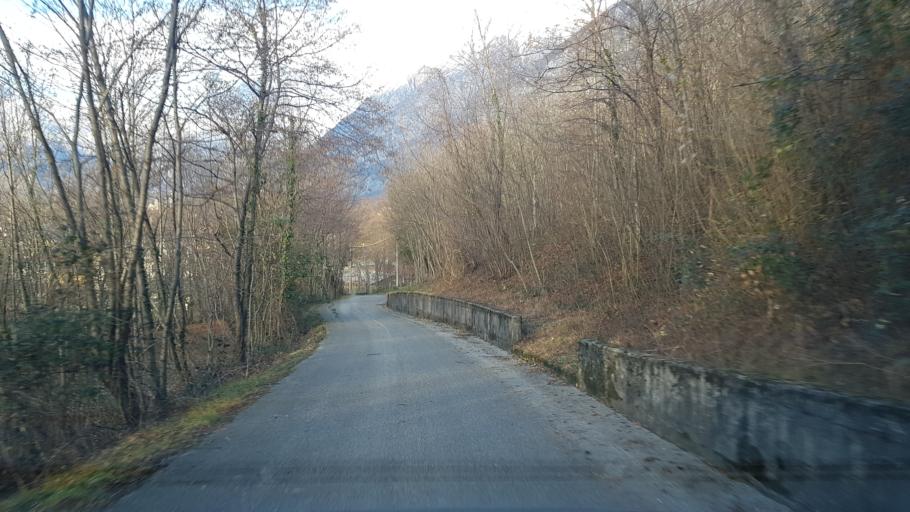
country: IT
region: Friuli Venezia Giulia
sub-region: Provincia di Udine
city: Venzone
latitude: 46.3244
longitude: 13.1412
